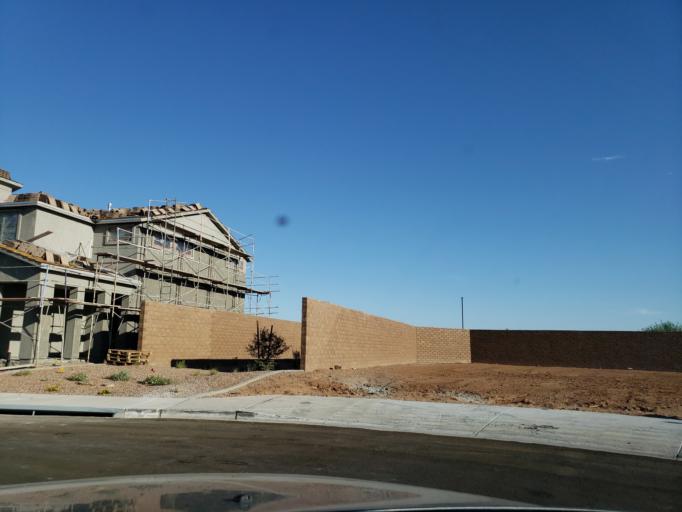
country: US
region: Arizona
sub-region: Maricopa County
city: Cave Creek
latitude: 33.6848
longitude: -112.0161
